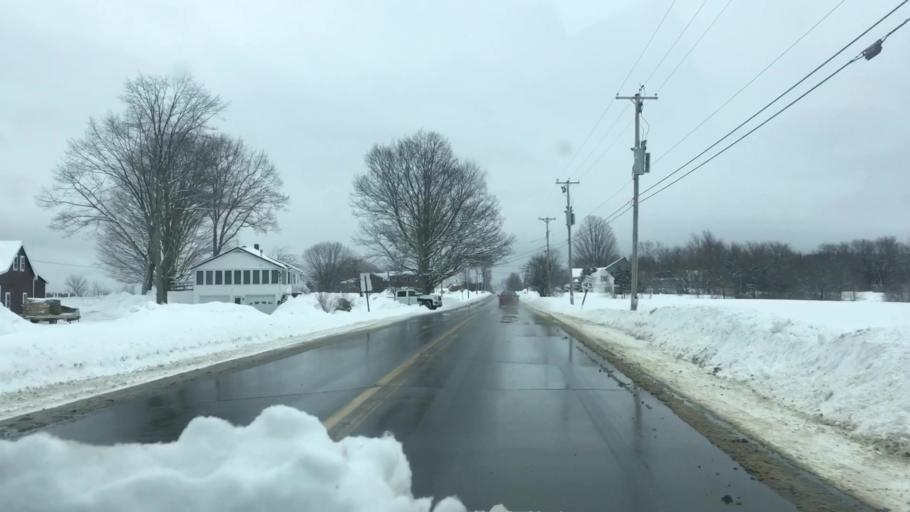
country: US
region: Maine
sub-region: Penobscot County
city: Charleston
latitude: 44.9955
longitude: -69.0512
